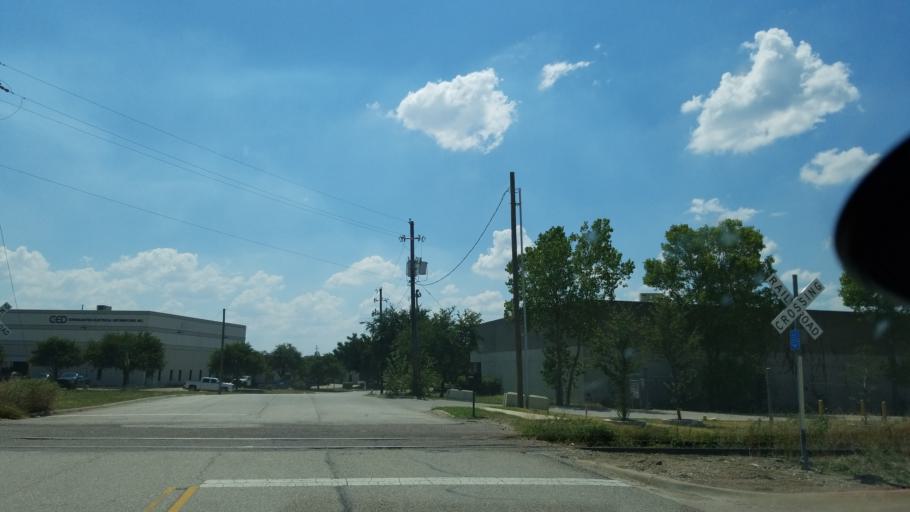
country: US
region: Texas
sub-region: Dallas County
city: Garland
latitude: 32.9011
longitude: -96.6942
